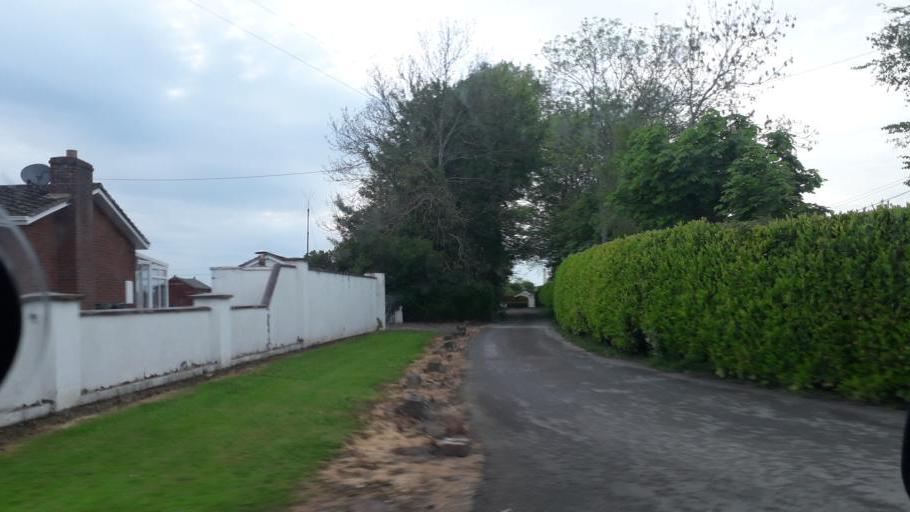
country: IE
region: Leinster
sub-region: Kildare
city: Celbridge
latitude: 53.3032
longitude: -6.5596
